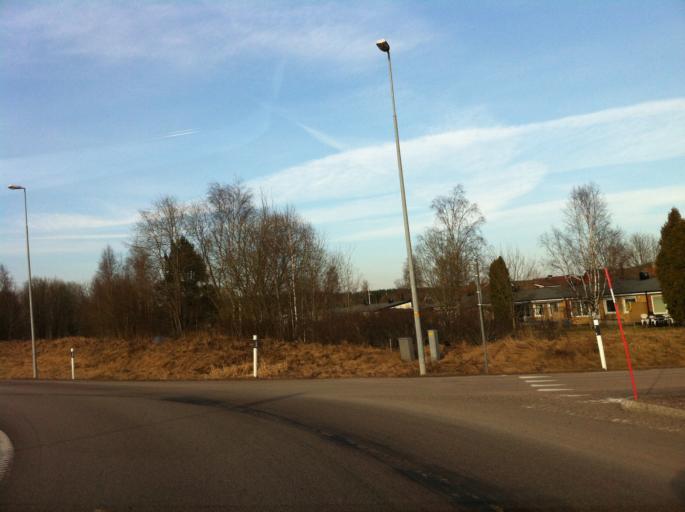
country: SE
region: Vaermland
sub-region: Storfors Kommun
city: Storfors
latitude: 59.5440
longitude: 14.2779
